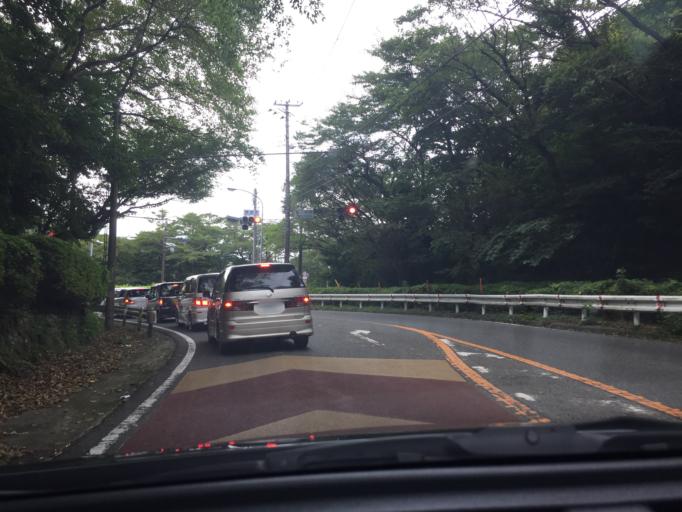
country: JP
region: Shizuoka
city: Ito
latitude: 34.9232
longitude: 139.1194
